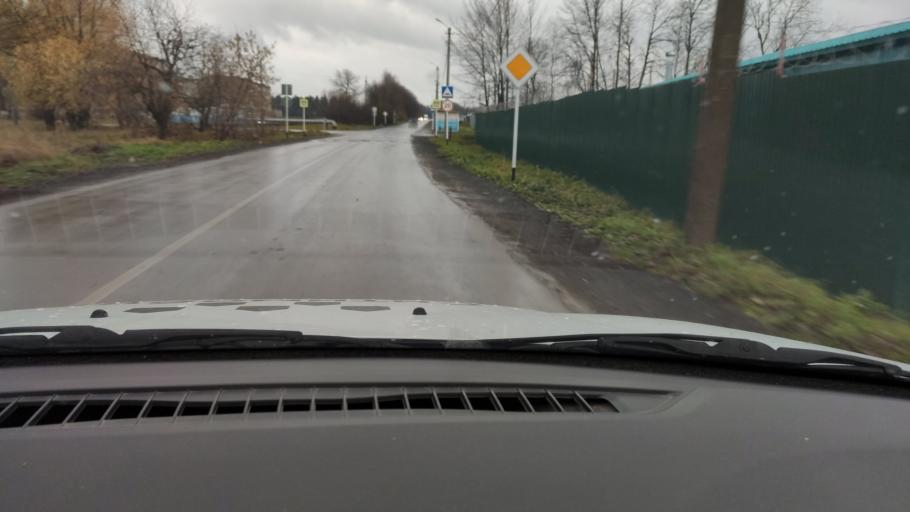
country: RU
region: Perm
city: Sylva
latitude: 58.0311
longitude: 56.7409
